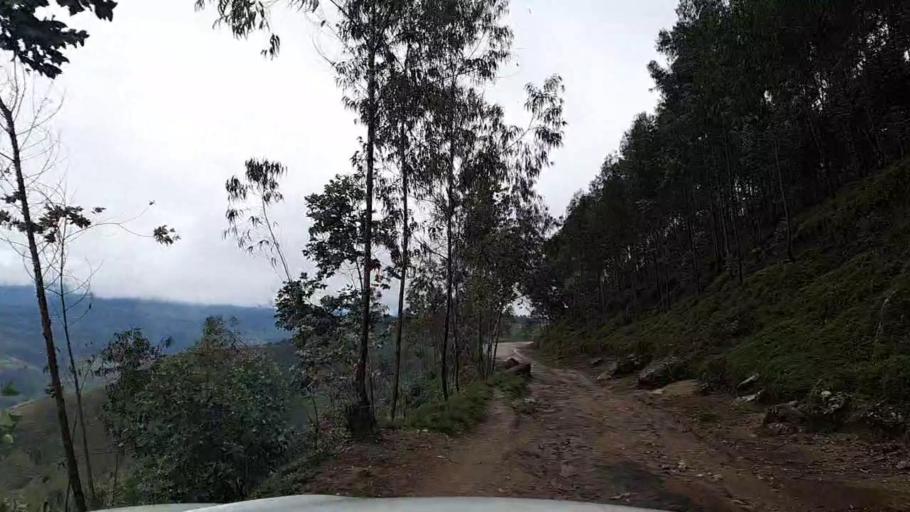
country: RW
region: Southern Province
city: Gikongoro
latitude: -2.3676
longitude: 29.4960
